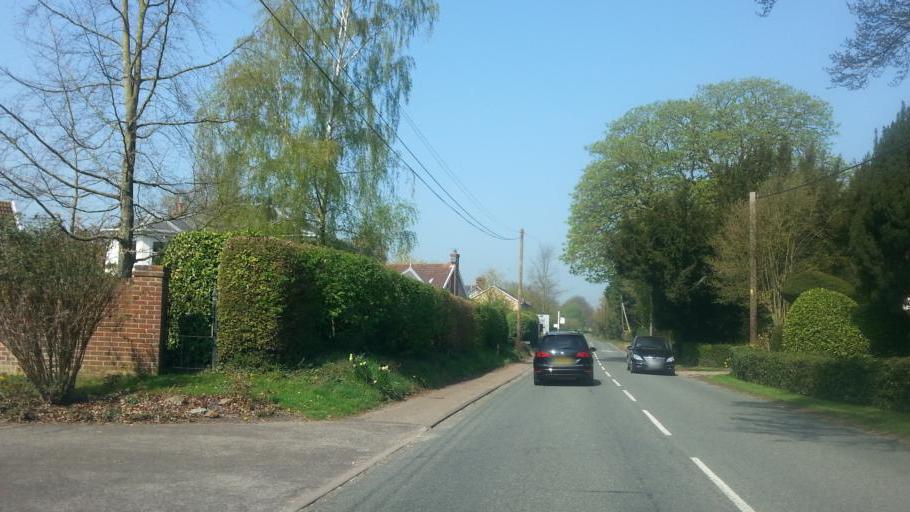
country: GB
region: England
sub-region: Suffolk
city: Thurston
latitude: 52.2327
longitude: 0.8377
